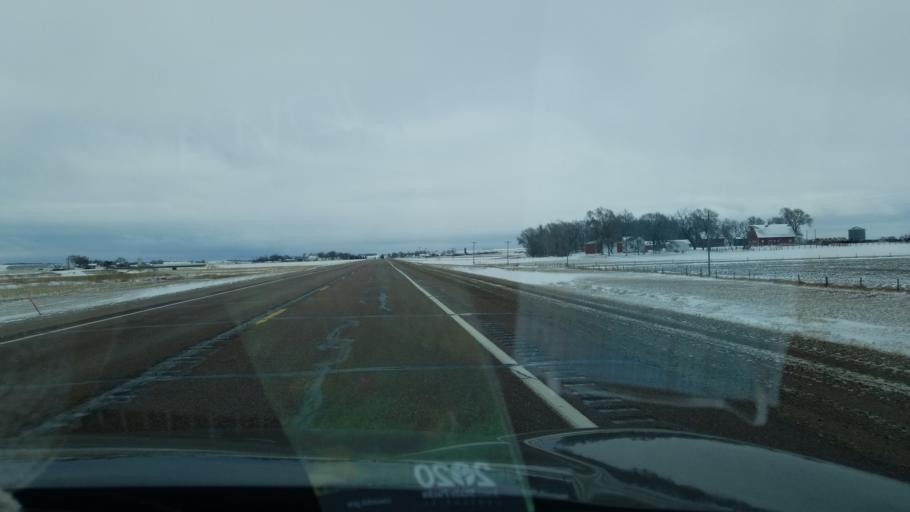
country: US
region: Iowa
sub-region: Plymouth County
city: Le Mars
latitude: 42.9184
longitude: -96.1749
